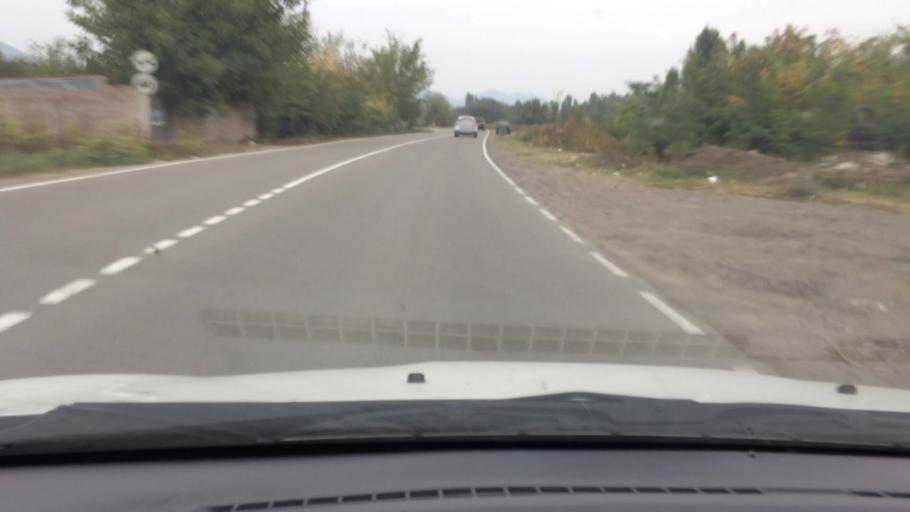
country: AM
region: Tavush
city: Bagratashen
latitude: 41.2565
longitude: 44.7979
